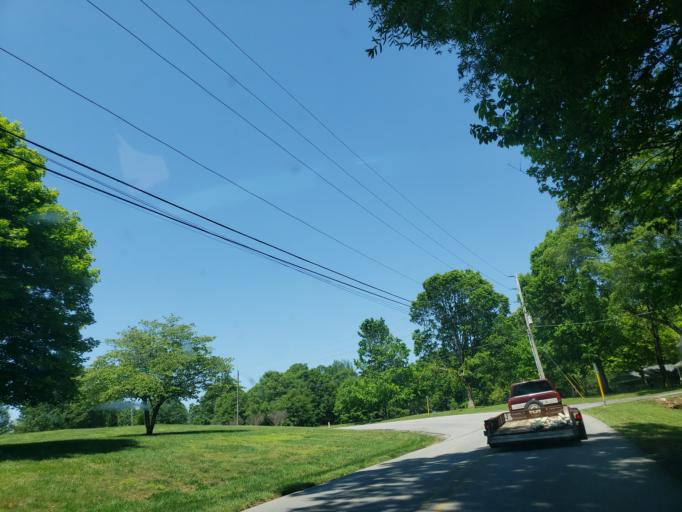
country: US
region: Alabama
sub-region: Madison County
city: Hazel Green
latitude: 34.9612
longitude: -86.5733
